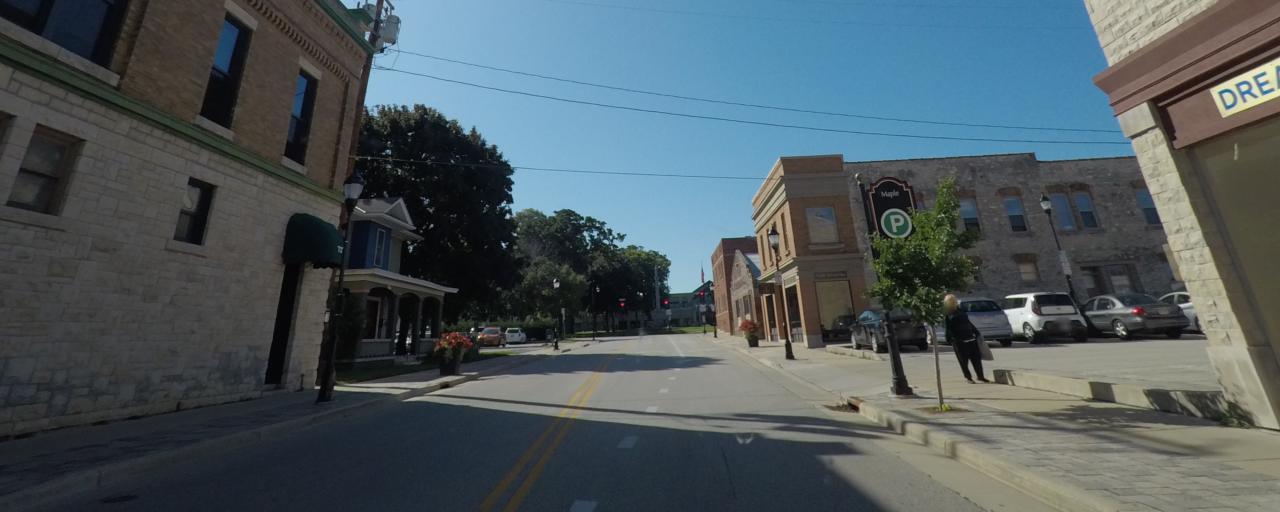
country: US
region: Wisconsin
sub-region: Waukesha County
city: Waukesha
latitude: 43.0107
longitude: -88.2328
